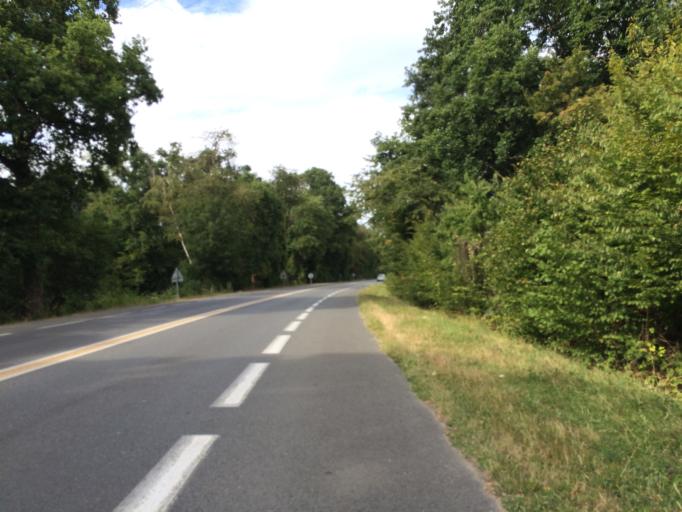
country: FR
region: Ile-de-France
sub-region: Departement de l'Essonne
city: Quincy-sous-Senart
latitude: 48.6751
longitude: 2.5249
